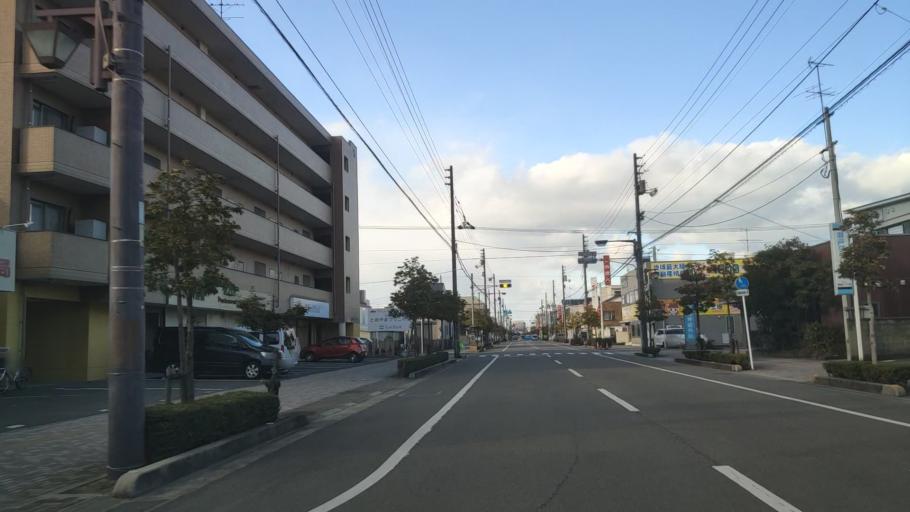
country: JP
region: Ehime
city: Saijo
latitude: 33.9161
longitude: 133.1862
